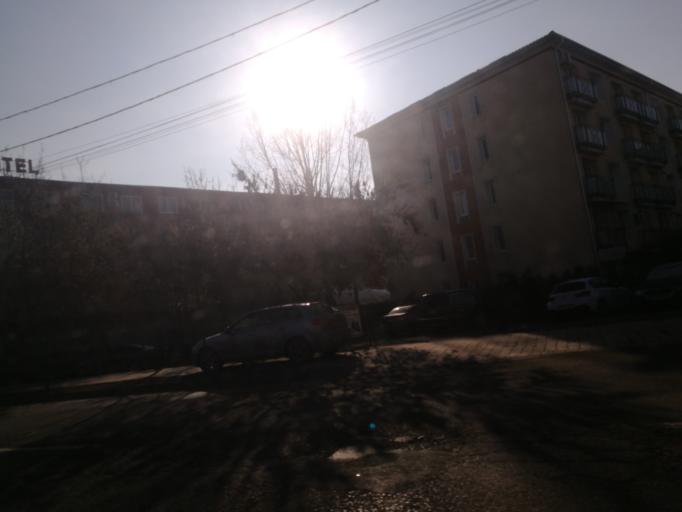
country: RO
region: Iasi
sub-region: Municipiul Iasi
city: Iasi
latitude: 47.1460
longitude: 27.5851
